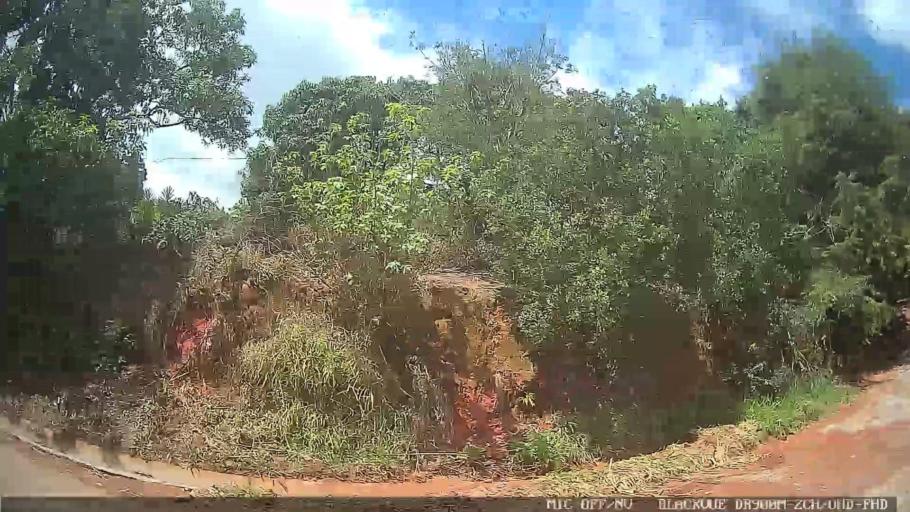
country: BR
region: Minas Gerais
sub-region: Extrema
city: Extrema
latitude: -22.8024
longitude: -46.4733
